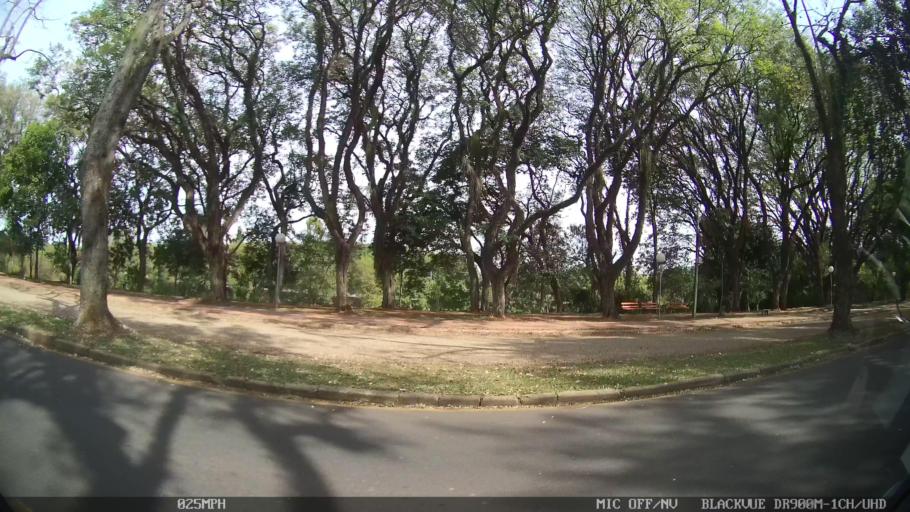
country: BR
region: Sao Paulo
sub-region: Piracicaba
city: Piracicaba
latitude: -22.7220
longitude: -47.6710
